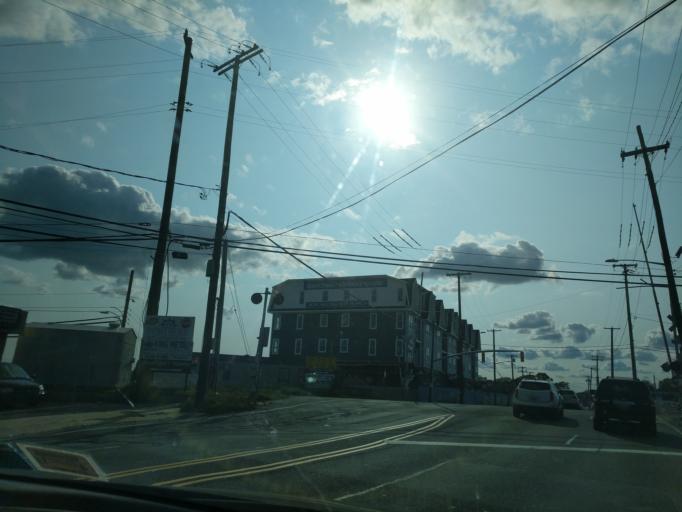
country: US
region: New York
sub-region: Nassau County
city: East Rockaway
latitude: 40.6409
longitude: -73.6565
